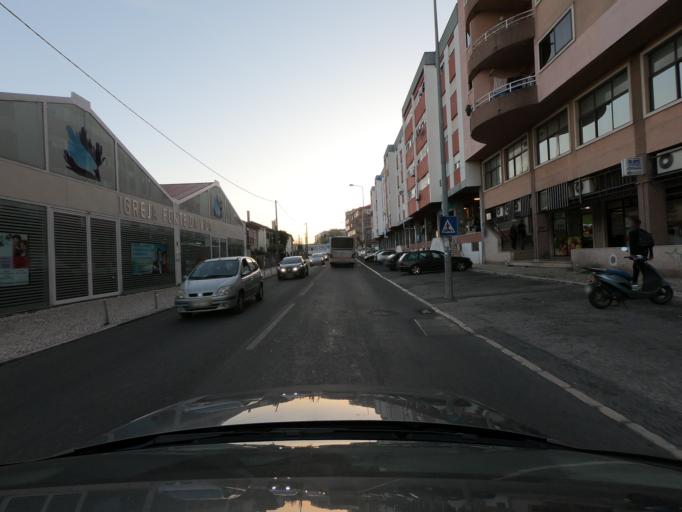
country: PT
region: Lisbon
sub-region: Sintra
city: Queluz
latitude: 38.7566
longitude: -9.2621
